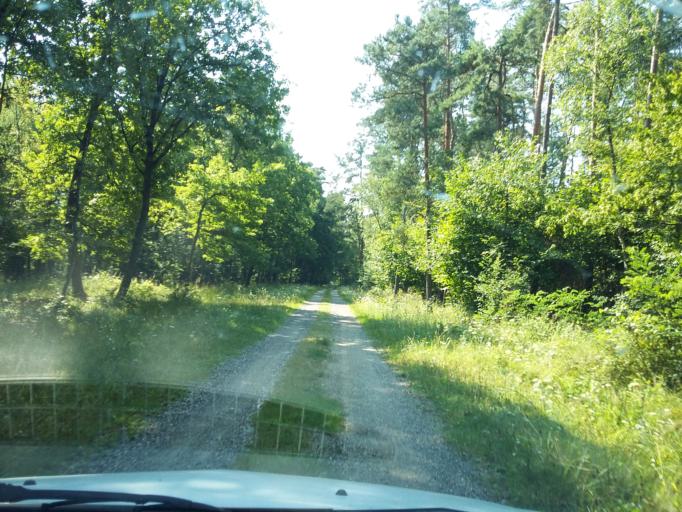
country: SI
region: Hodos-Hodos
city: Hodos
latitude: 46.8547
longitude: 16.3176
